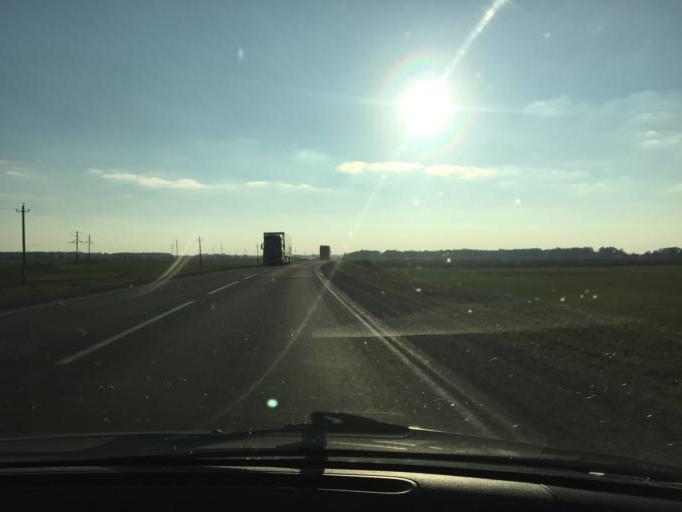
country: BY
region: Brest
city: Asnyezhytsy
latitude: 52.2796
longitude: 26.4009
